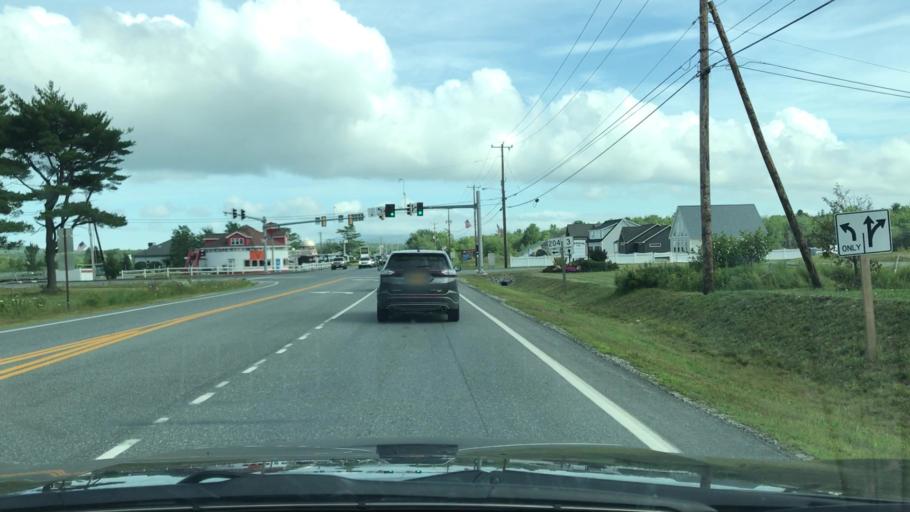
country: US
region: Maine
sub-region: Hancock County
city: Trenton
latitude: 44.4891
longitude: -68.3716
